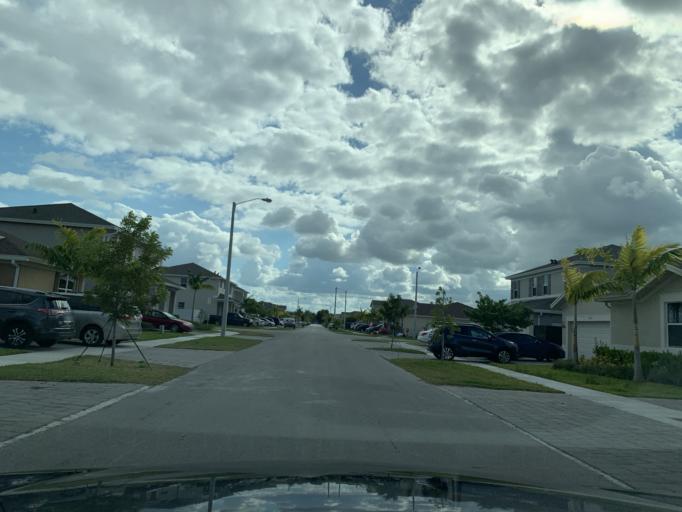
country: US
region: Florida
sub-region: Miami-Dade County
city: Naranja
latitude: 25.5099
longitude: -80.4075
